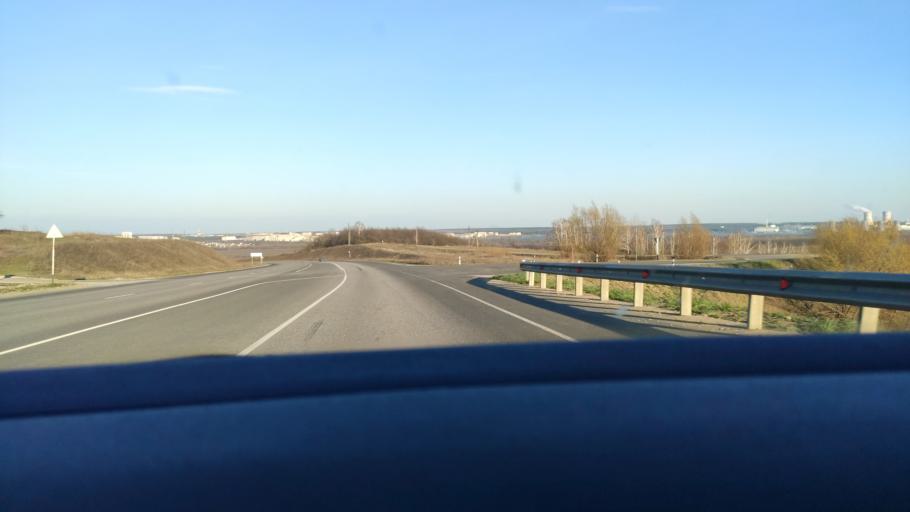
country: RU
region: Voronezj
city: Kolodeznyy
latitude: 51.3284
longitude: 39.1447
